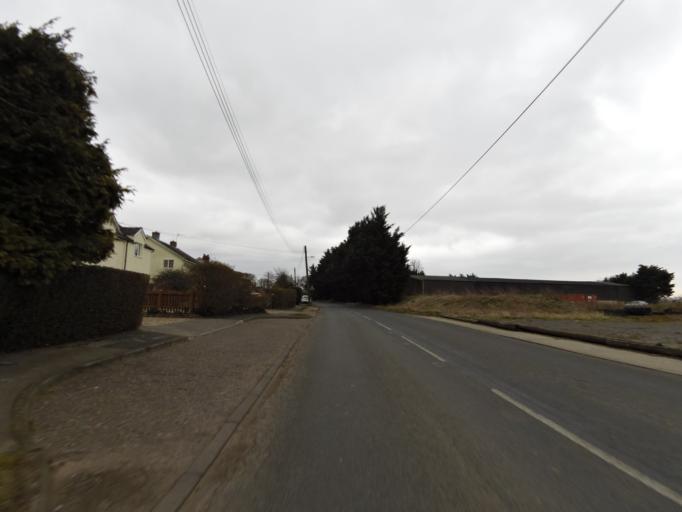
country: GB
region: England
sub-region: Suffolk
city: Ipswich
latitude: 52.1198
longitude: 1.1494
